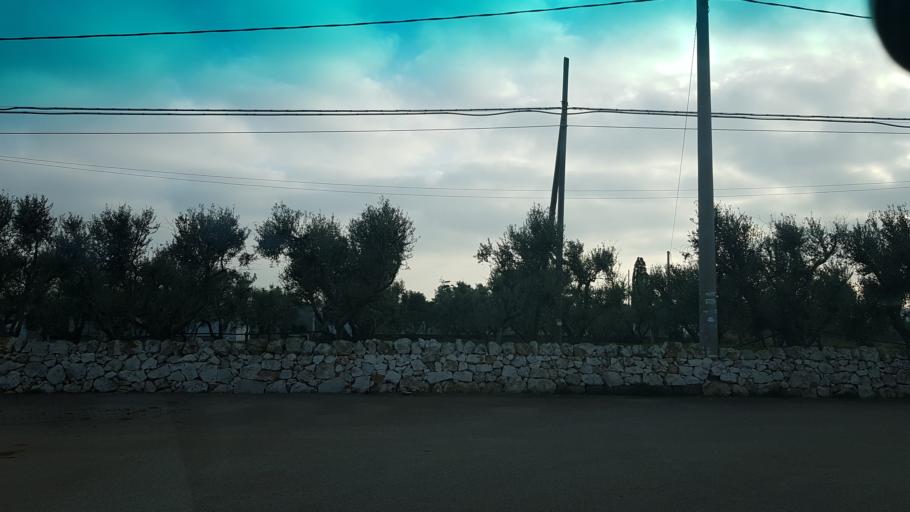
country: IT
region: Apulia
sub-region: Provincia di Brindisi
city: Carovigno
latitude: 40.7426
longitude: 17.7235
